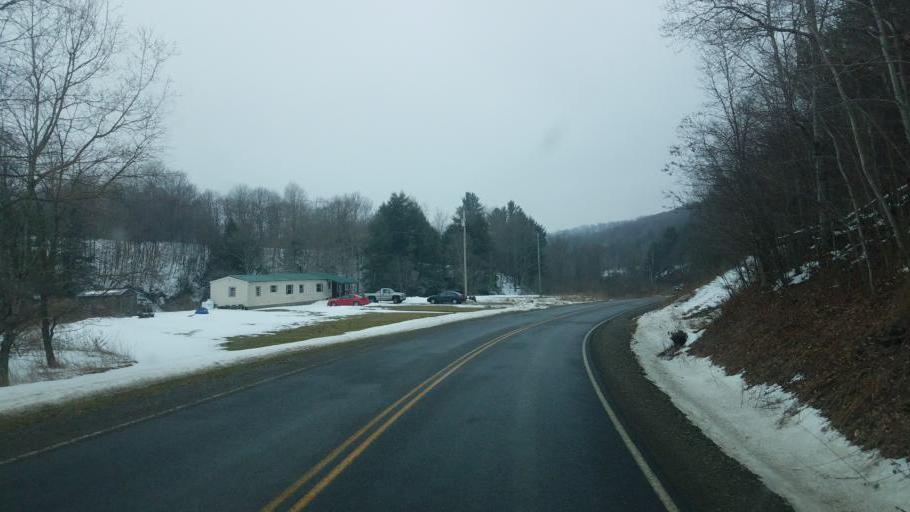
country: US
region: New York
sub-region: Allegany County
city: Andover
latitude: 42.0250
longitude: -77.7303
